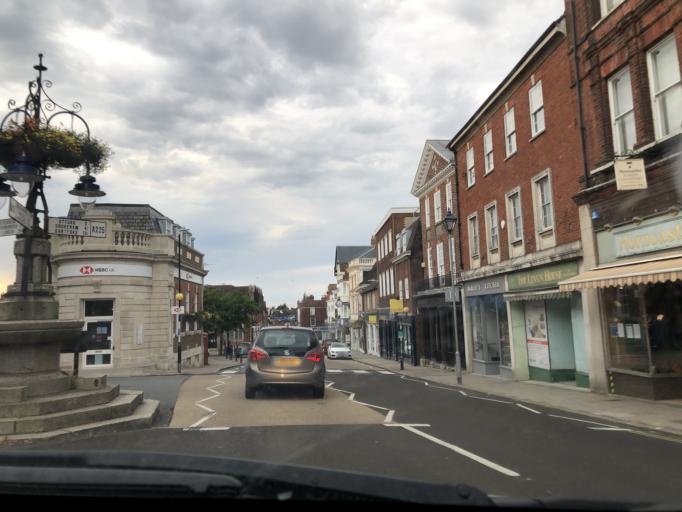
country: GB
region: England
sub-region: Kent
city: Sevenoaks
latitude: 51.2694
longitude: 0.1932
